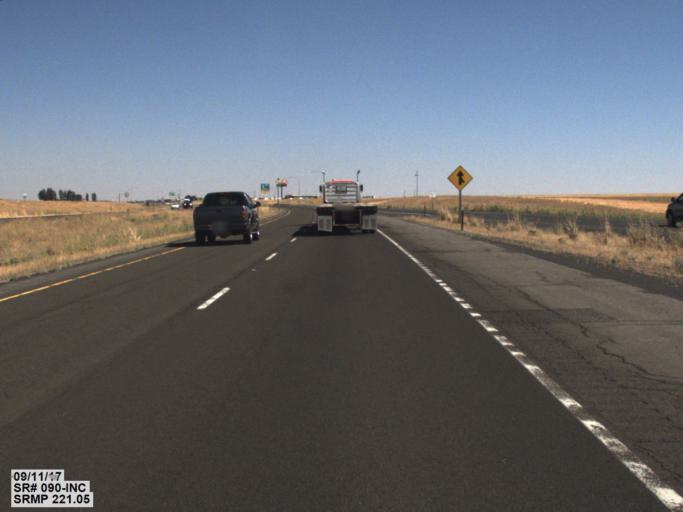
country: US
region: Washington
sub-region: Adams County
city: Ritzville
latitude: 47.1113
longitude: -118.3836
